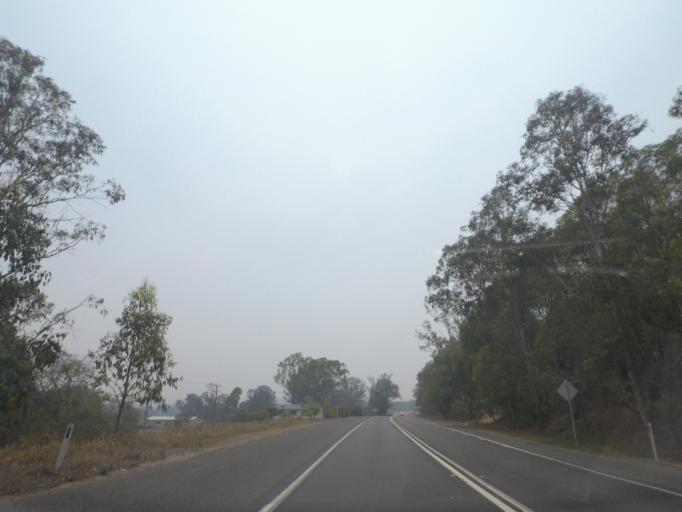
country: AU
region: New South Wales
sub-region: Clarence Valley
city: Maclean
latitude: -29.5539
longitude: 153.1528
